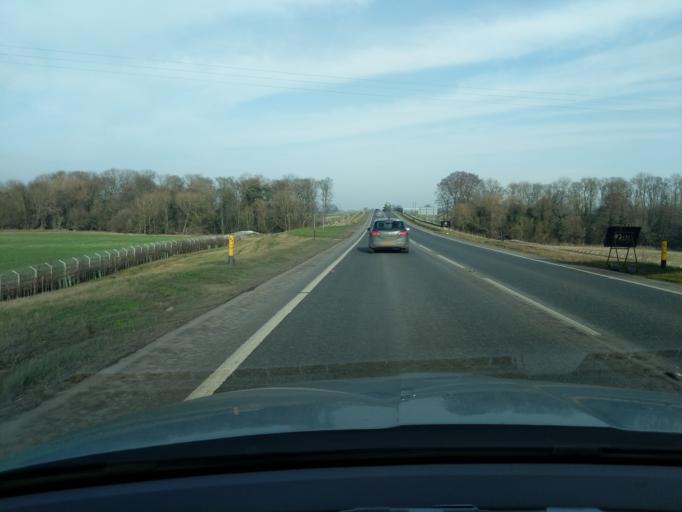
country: GB
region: England
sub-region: North Yorkshire
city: Bedale
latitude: 54.2936
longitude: -1.5957
